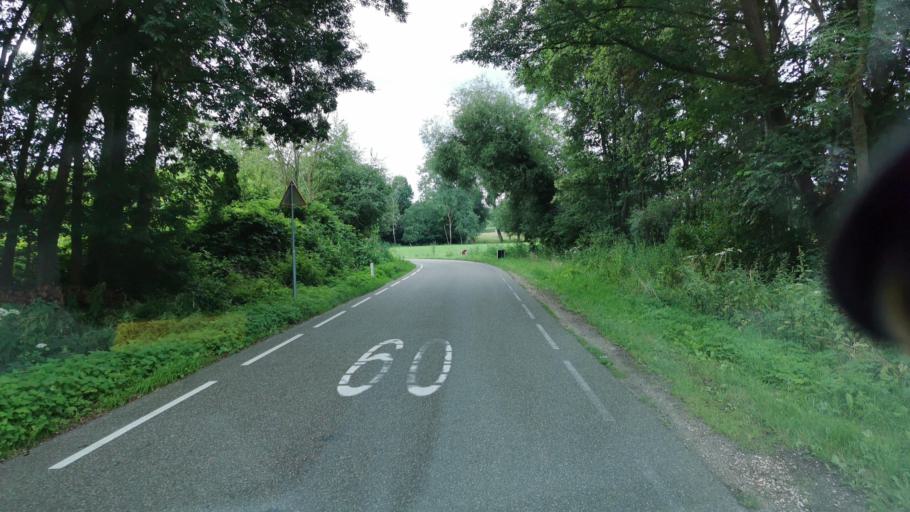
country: NL
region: Overijssel
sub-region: Gemeente Enschede
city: Enschede
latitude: 52.2478
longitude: 6.9307
